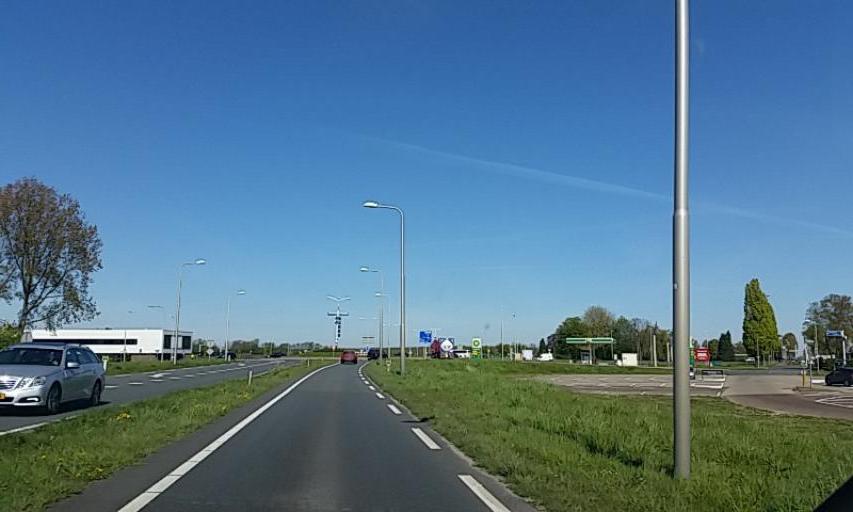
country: NL
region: Zeeland
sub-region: Gemeente Hulst
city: Hulst
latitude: 51.2732
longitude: 4.0410
